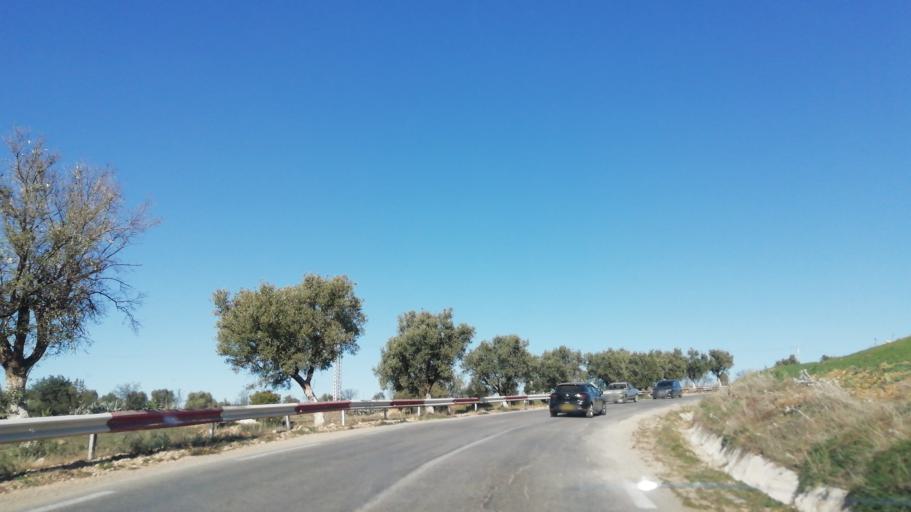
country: DZ
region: Tlemcen
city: Beni Mester
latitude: 34.8325
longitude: -1.5048
